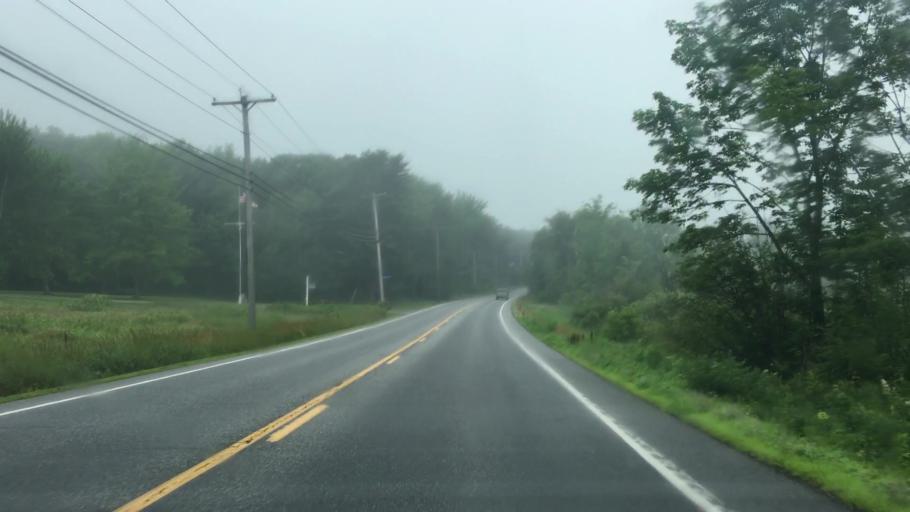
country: US
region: Maine
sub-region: Lincoln County
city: Boothbay
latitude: 43.8883
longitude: -69.6295
